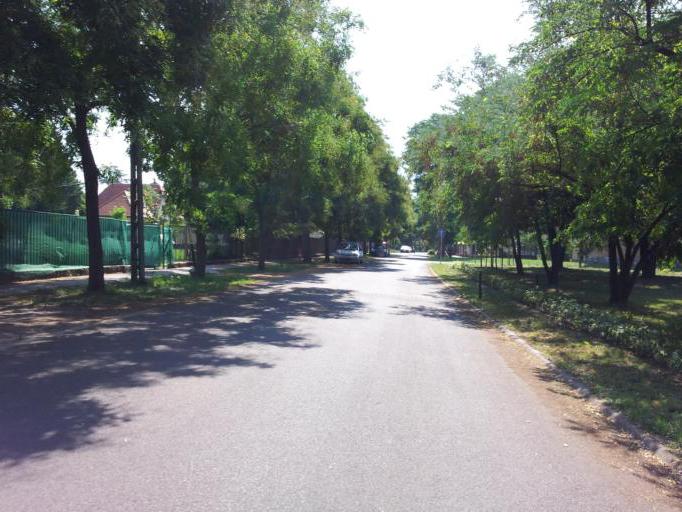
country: HU
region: Budapest
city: Budapest XIV. keruelet
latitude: 47.5117
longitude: 19.1184
